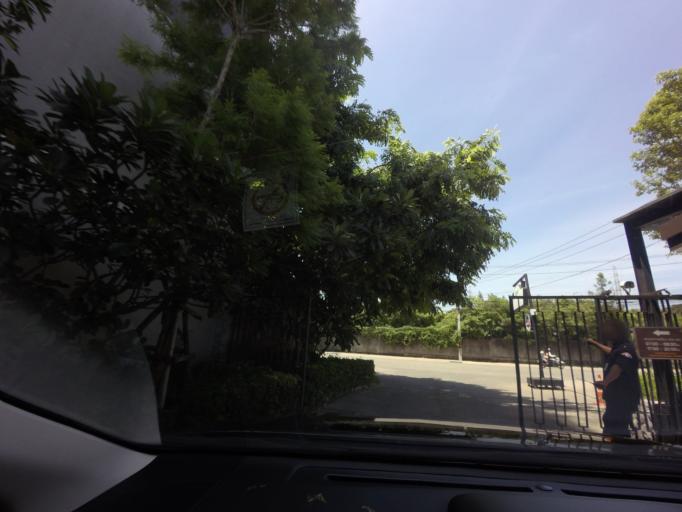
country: TH
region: Chon Buri
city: Si Racha
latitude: 13.1598
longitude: 100.9402
